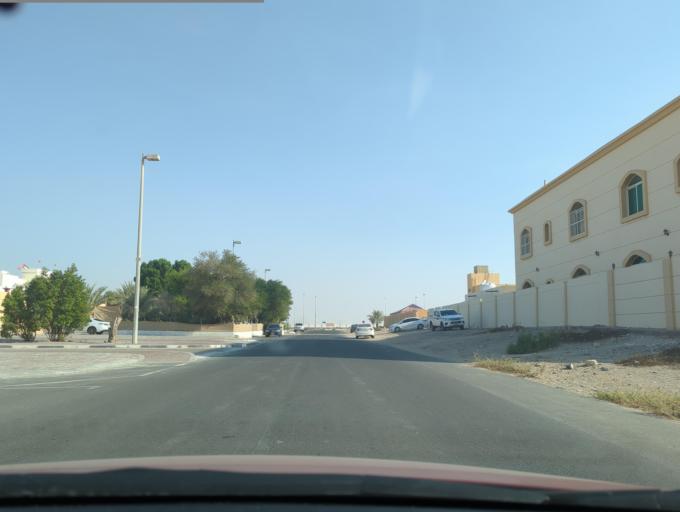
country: AE
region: Abu Dhabi
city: Abu Dhabi
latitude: 24.3967
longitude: 54.7435
